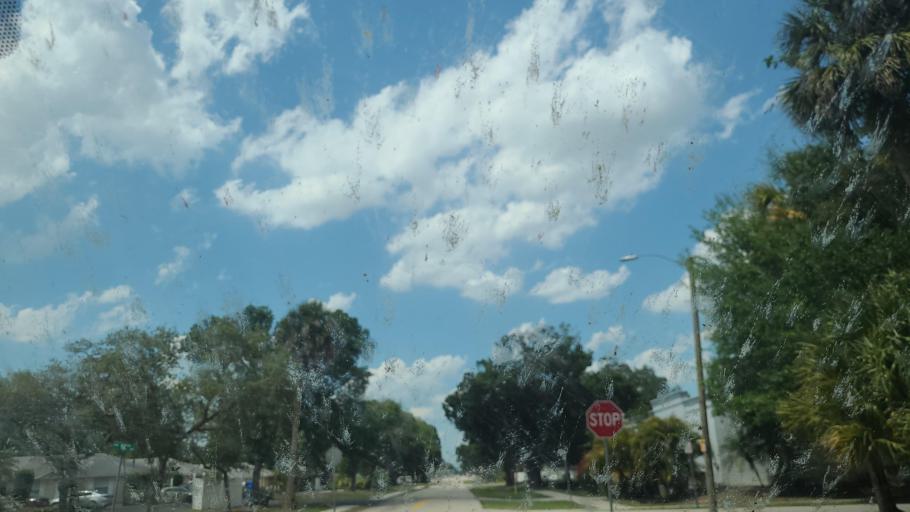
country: US
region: Florida
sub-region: Okeechobee County
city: Okeechobee
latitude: 27.2322
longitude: -80.8310
